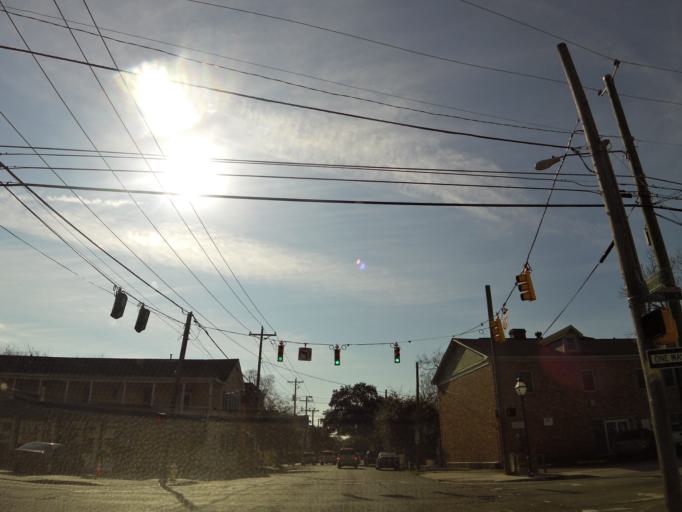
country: US
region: South Carolina
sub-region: Charleston County
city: Charleston
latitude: 32.7904
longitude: -79.9474
